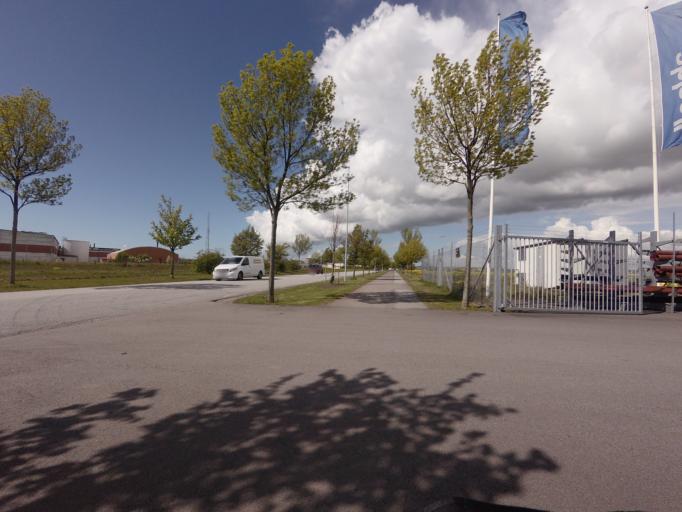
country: SE
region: Skane
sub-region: Landskrona
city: Landskrona
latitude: 55.8842
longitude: 12.8543
